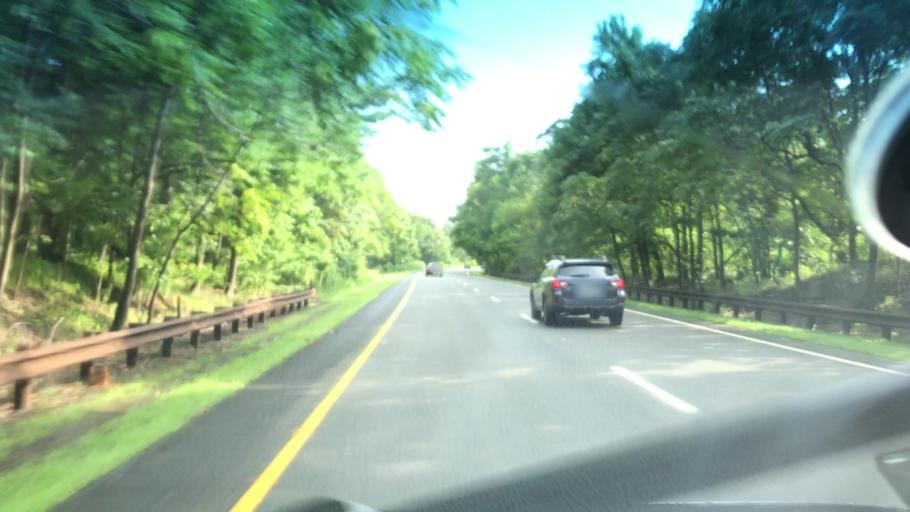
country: US
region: New Jersey
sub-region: Bergen County
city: Englewood Cliffs
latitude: 40.9022
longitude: -73.9370
